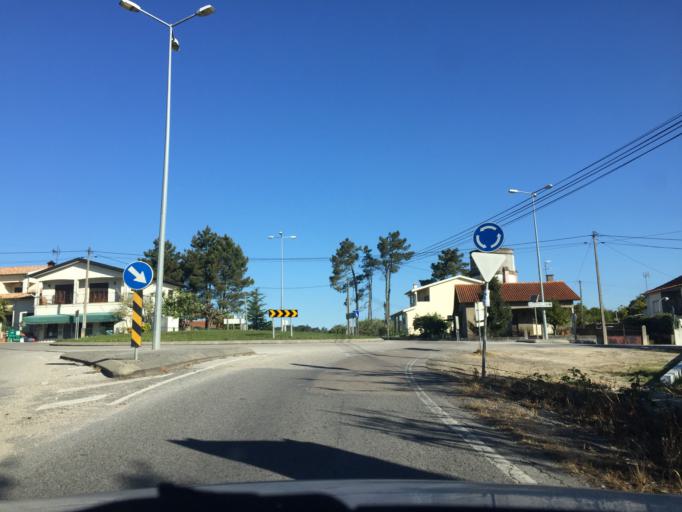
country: PT
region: Aveiro
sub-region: Anadia
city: Arcos
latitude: 40.4484
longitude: -8.4680
